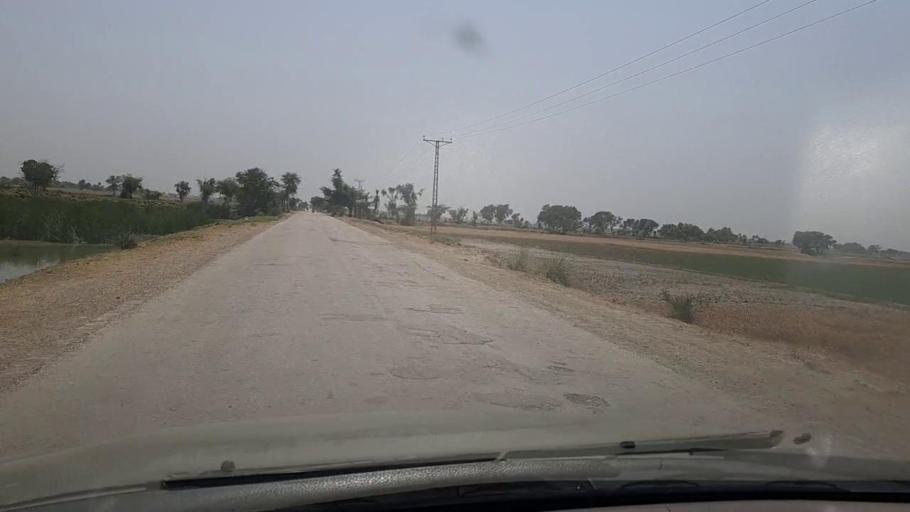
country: PK
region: Sindh
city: Miro Khan
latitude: 27.7112
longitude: 68.0650
